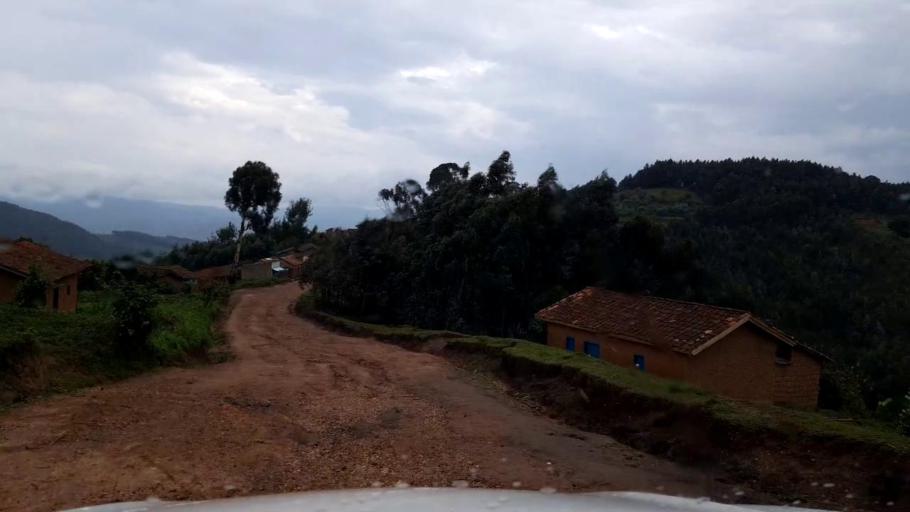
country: RW
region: Western Province
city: Kibuye
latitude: -2.0233
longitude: 29.4561
